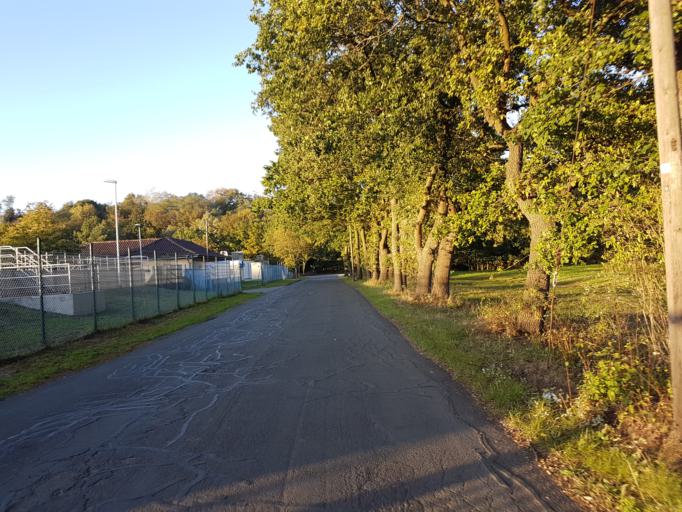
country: DE
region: Lower Saxony
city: Langenhagen
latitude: 52.4427
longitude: 9.7670
